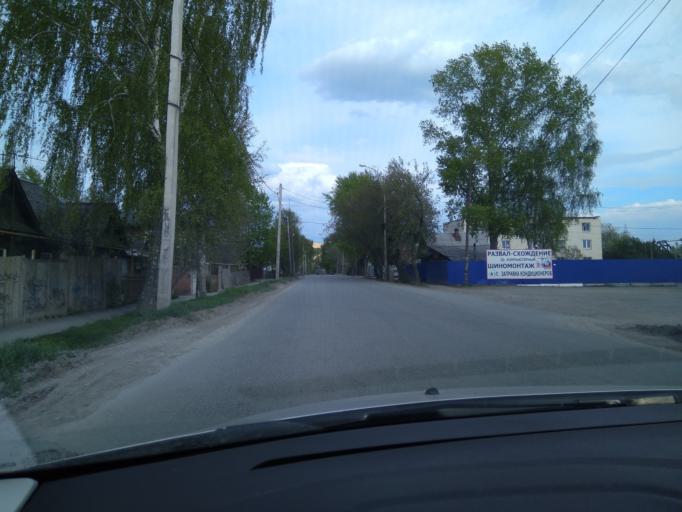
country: RU
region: Sverdlovsk
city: Yekaterinburg
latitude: 56.8815
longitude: 60.5538
